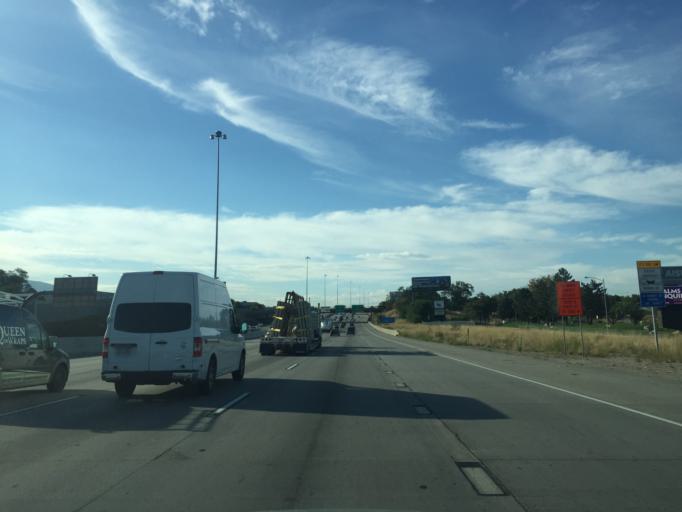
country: US
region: Utah
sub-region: Salt Lake County
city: Murray
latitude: 40.6640
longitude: -111.9016
